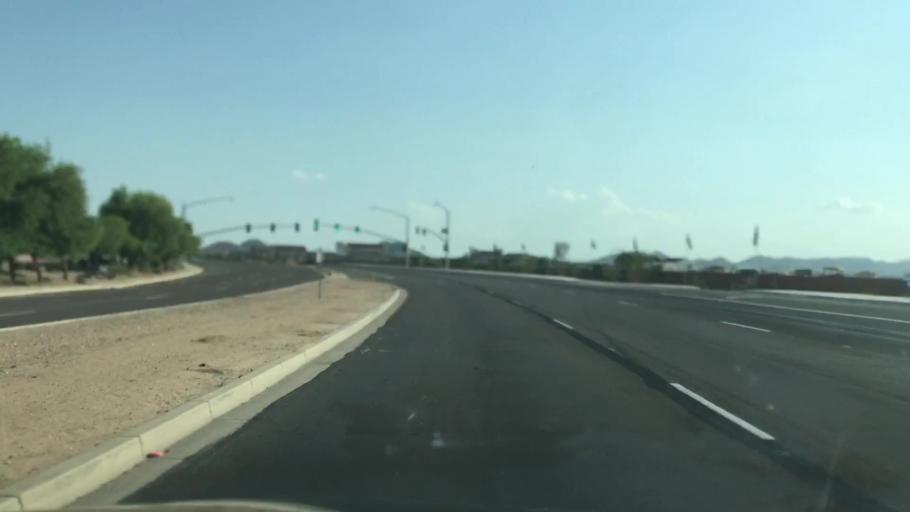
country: US
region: Arizona
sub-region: Pinal County
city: San Tan Valley
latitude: 33.2104
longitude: -111.5651
